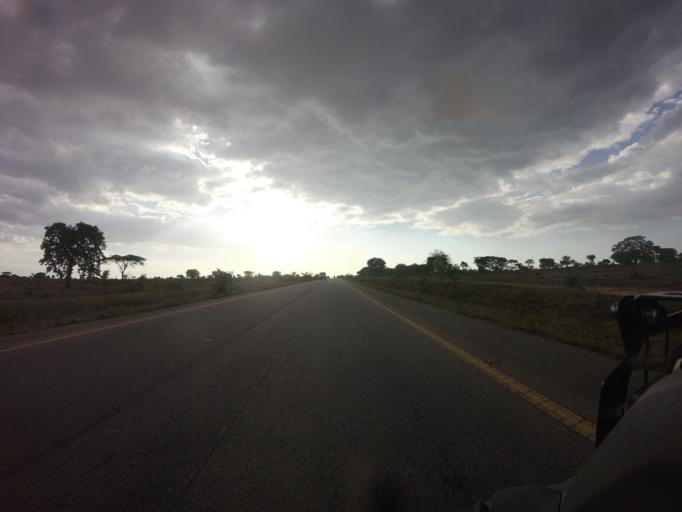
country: AO
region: Huila
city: Lubango
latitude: -14.6046
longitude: 14.0060
